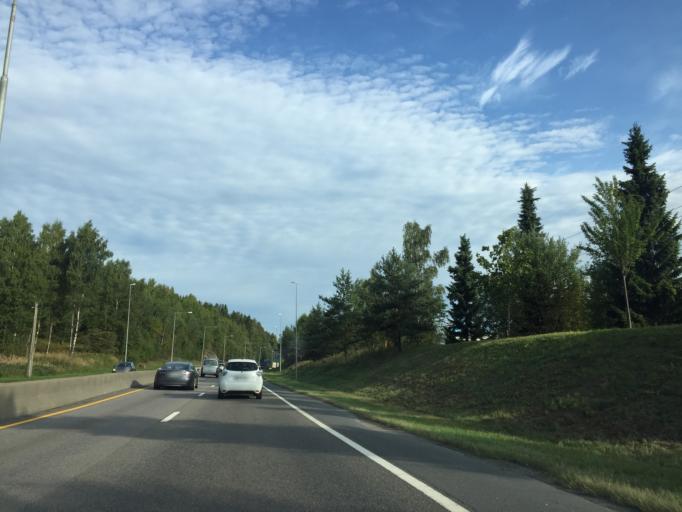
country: NO
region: Akershus
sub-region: Oppegard
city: Kolbotn
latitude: 59.8708
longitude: 10.8278
